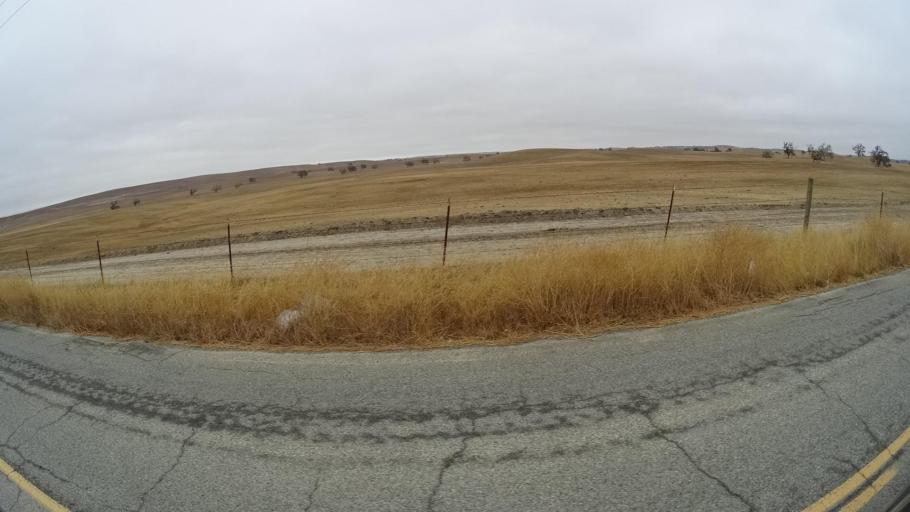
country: US
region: California
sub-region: San Luis Obispo County
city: Lake Nacimiento
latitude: 35.8423
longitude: -120.8428
